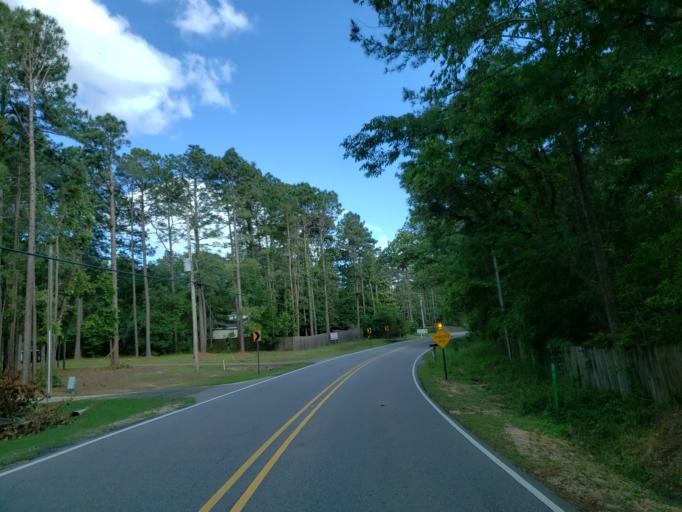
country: US
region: Mississippi
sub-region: Lamar County
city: West Hattiesburg
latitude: 31.2851
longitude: -89.4376
